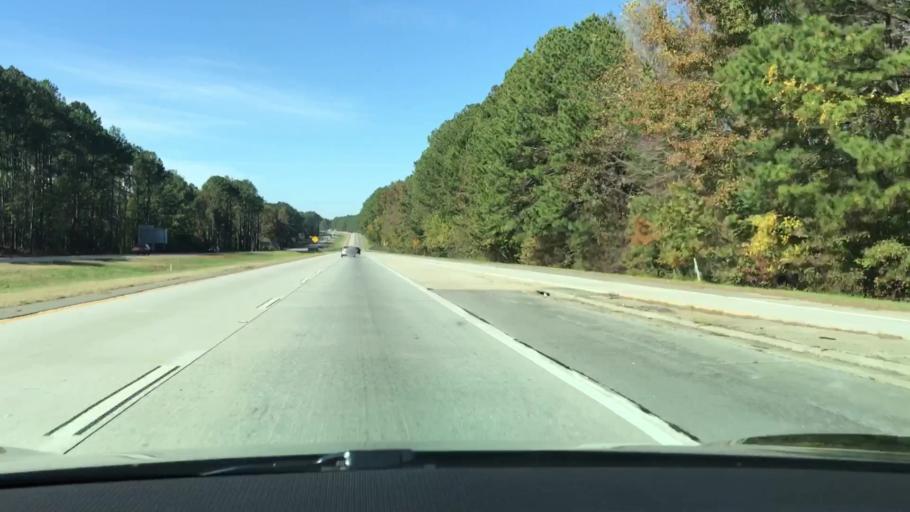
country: US
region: Georgia
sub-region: Taliaferro County
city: Crawfordville
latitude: 33.5301
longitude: -82.9147
